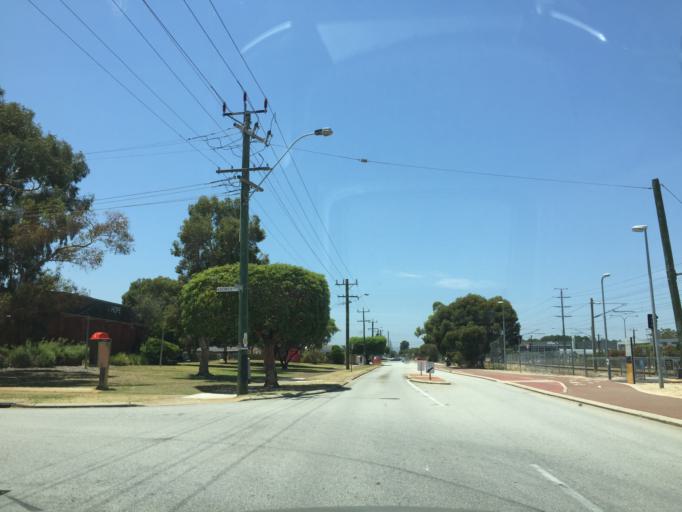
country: AU
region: Western Australia
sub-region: Canning
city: Queens Park
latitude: -32.0076
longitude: 115.9394
